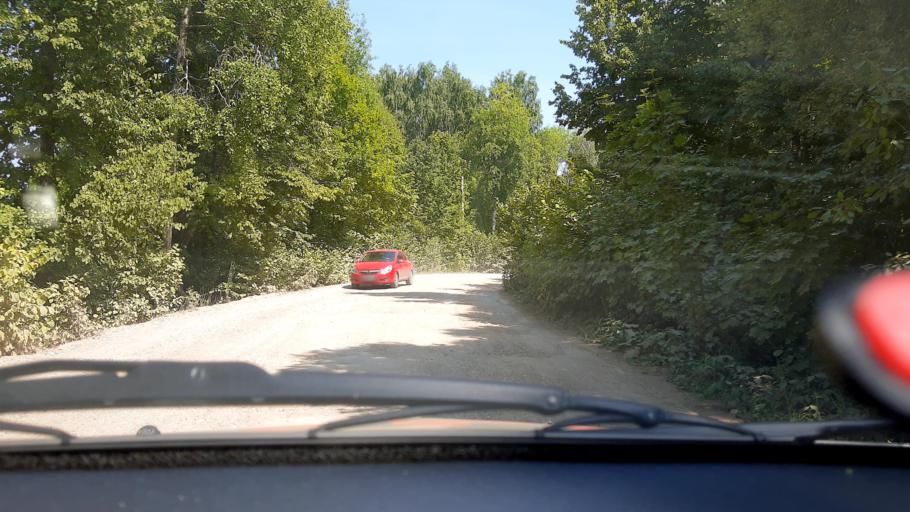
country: RU
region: Bashkortostan
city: Karmaskaly
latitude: 54.3869
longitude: 55.9076
